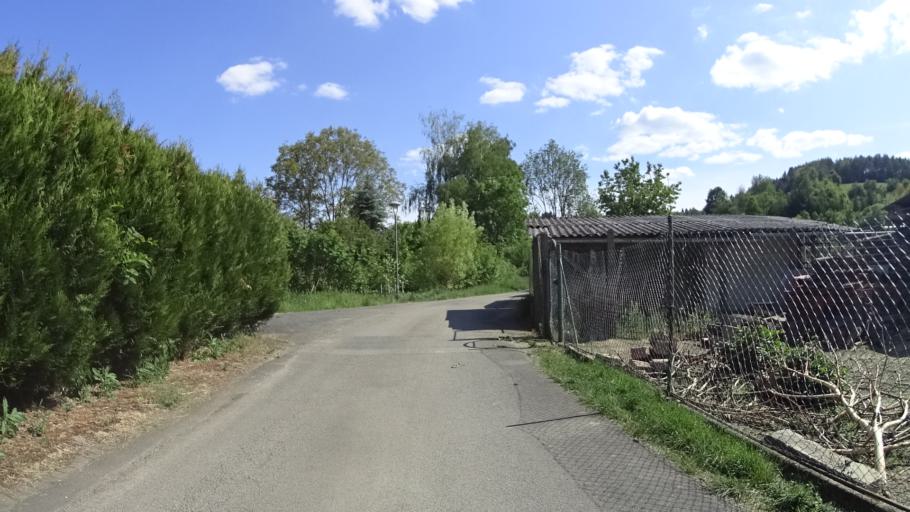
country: DE
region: Baden-Wuerttemberg
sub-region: Karlsruhe Region
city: Hardheim
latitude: 49.5785
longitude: 9.4859
